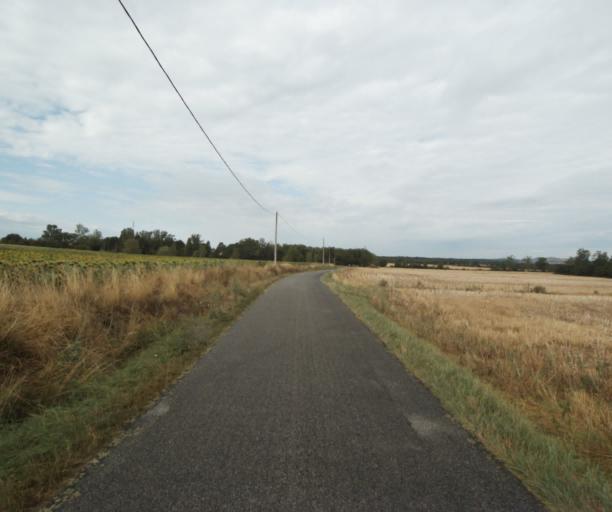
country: FR
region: Midi-Pyrenees
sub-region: Departement de la Haute-Garonne
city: Revel
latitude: 43.4210
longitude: 1.9720
